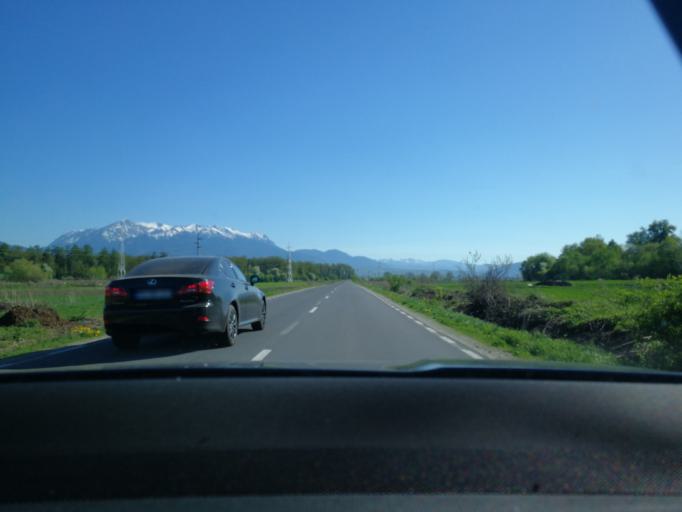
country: RO
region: Brasov
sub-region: Comuna Vulcan
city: Vulcan
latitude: 45.6009
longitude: 25.4201
